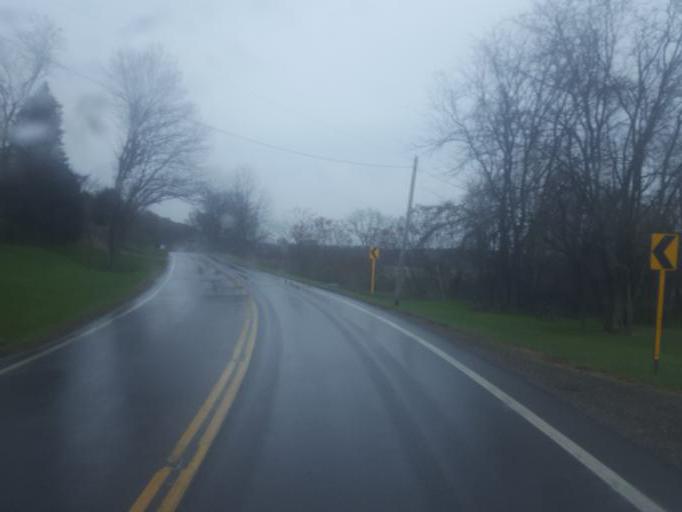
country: US
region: Ohio
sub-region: Ashland County
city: Loudonville
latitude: 40.7021
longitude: -82.3361
